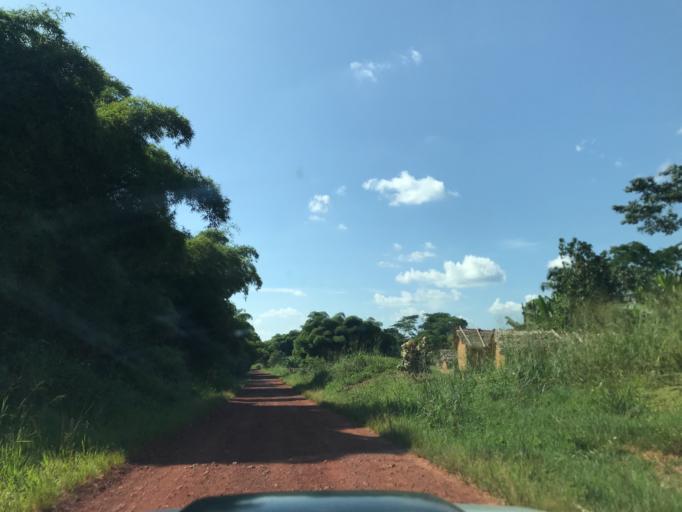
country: CD
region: Eastern Province
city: Kisangani
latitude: 1.2764
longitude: 25.2780
